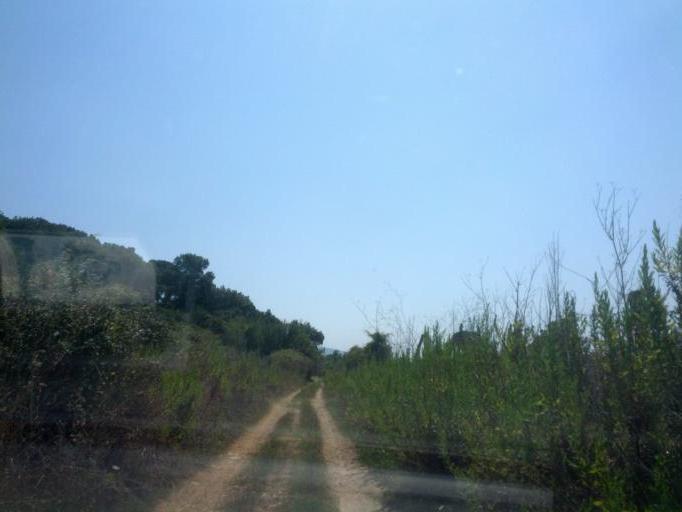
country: IT
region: Latium
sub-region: Provincia di Latina
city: Monte San Biagio
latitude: 41.3648
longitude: 13.3568
